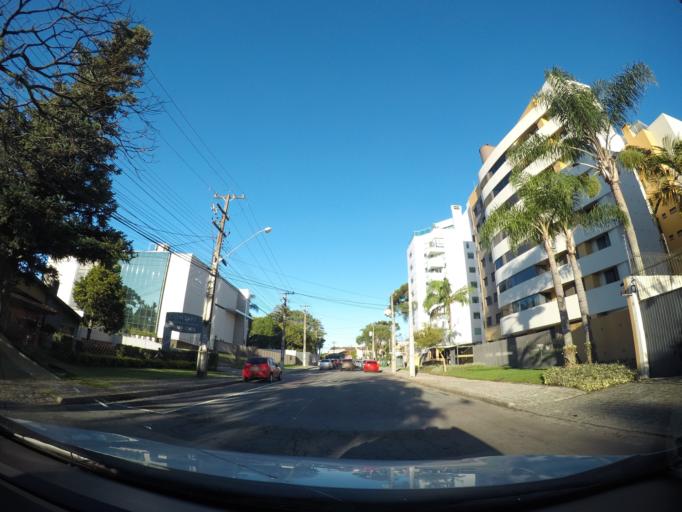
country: BR
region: Parana
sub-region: Curitiba
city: Curitiba
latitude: -25.4124
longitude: -49.2521
